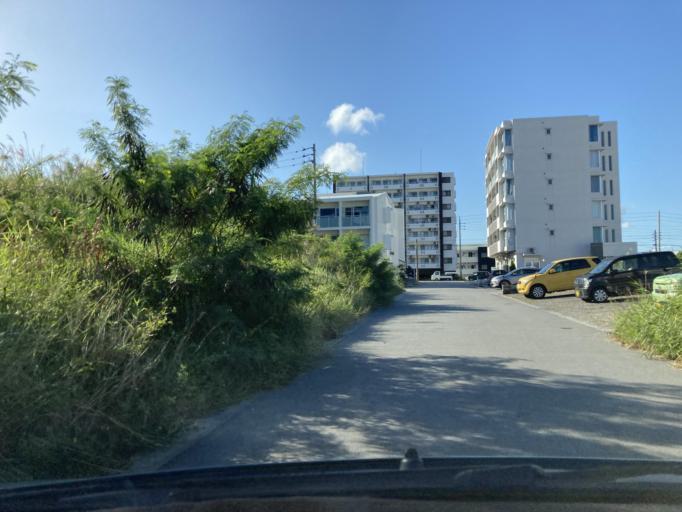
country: JP
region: Okinawa
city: Ginowan
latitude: 26.2370
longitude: 127.7266
